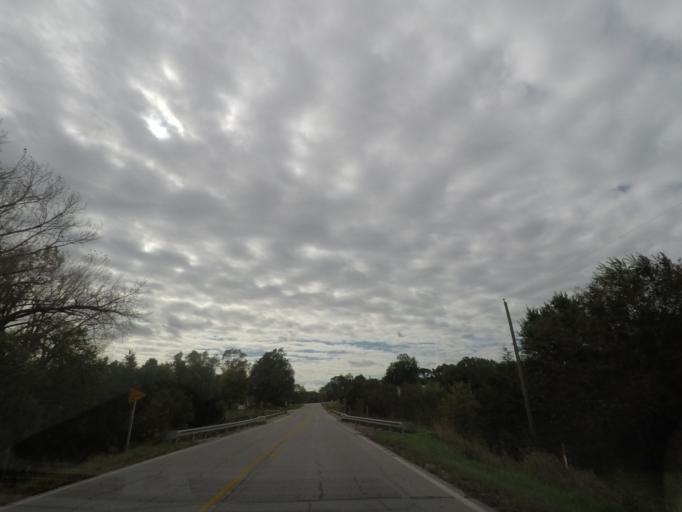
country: US
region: Iowa
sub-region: Story County
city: Huxley
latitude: 41.8367
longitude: -93.5325
